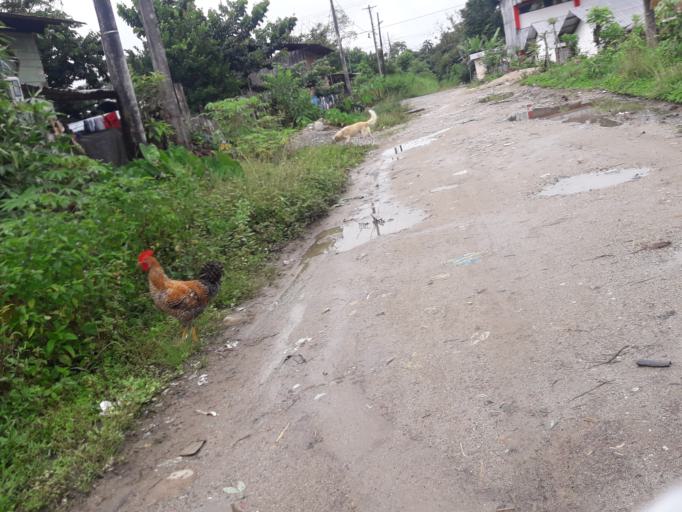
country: EC
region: Napo
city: Tena
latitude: -0.9661
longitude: -77.8539
